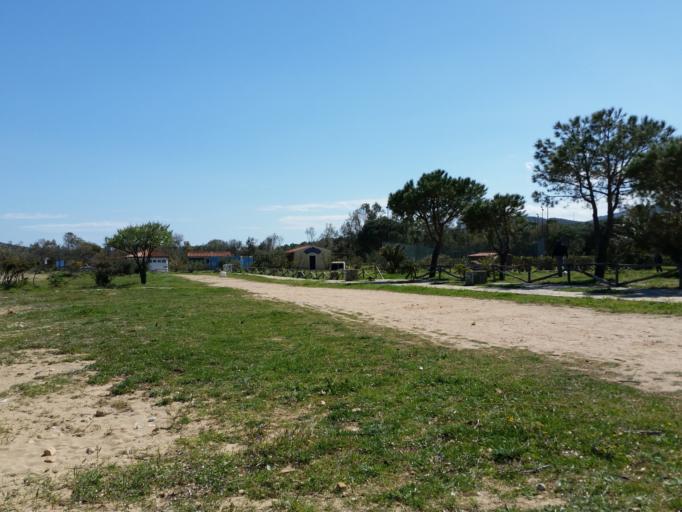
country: IT
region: Sardinia
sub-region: Provincia di Olbia-Tempio
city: Golfo Arnaci
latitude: 40.8797
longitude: 9.6362
